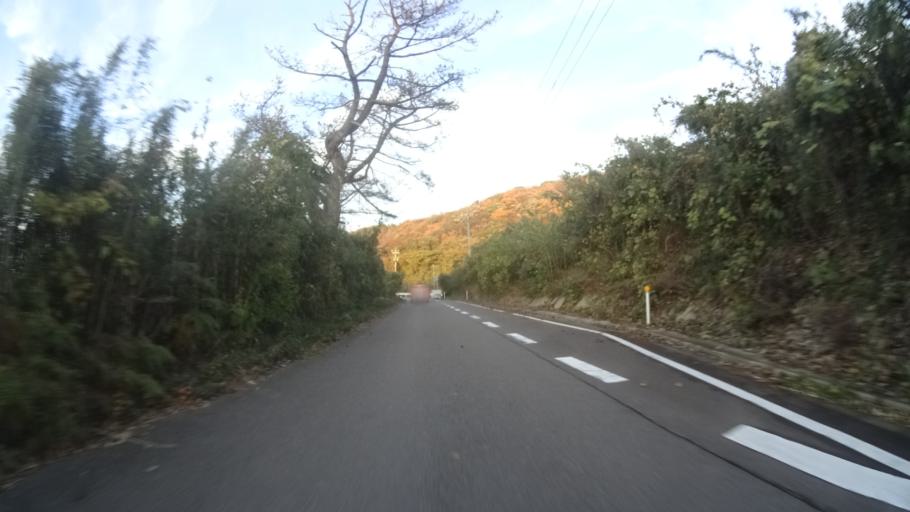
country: JP
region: Ishikawa
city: Nanao
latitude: 37.2152
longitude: 136.6947
